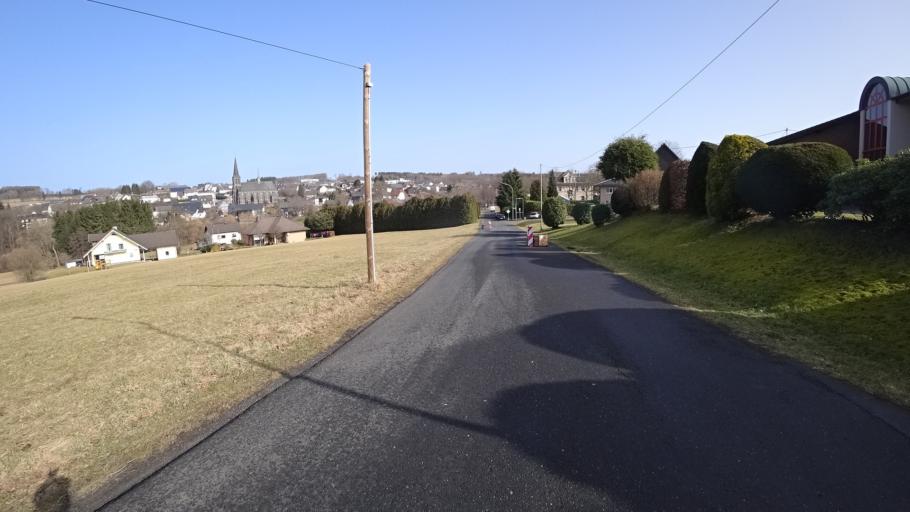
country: DE
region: Rheinland-Pfalz
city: Luckenbach
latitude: 50.7092
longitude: 7.8480
